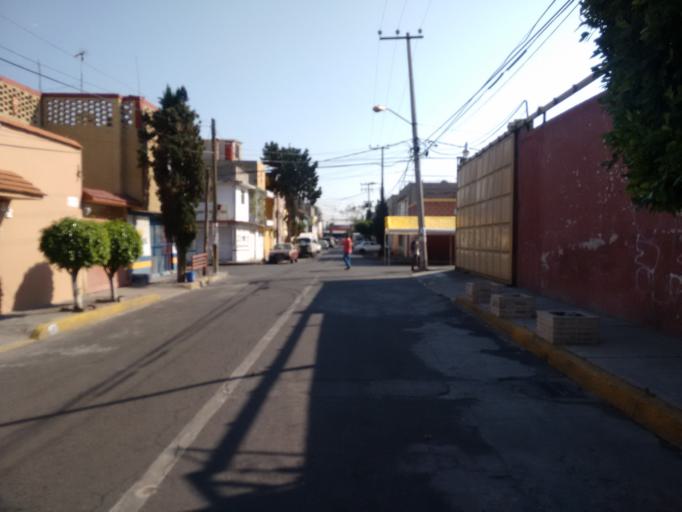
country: MX
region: Mexico City
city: Gustavo A. Madero
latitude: 19.4838
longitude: -99.0451
